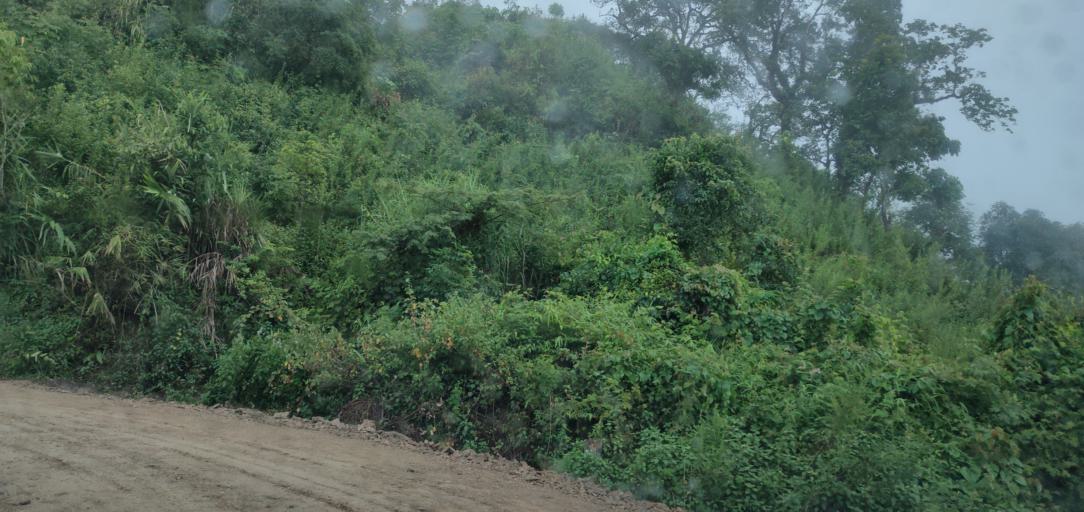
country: LA
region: Phongsali
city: Phongsali
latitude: 21.4321
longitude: 102.1595
